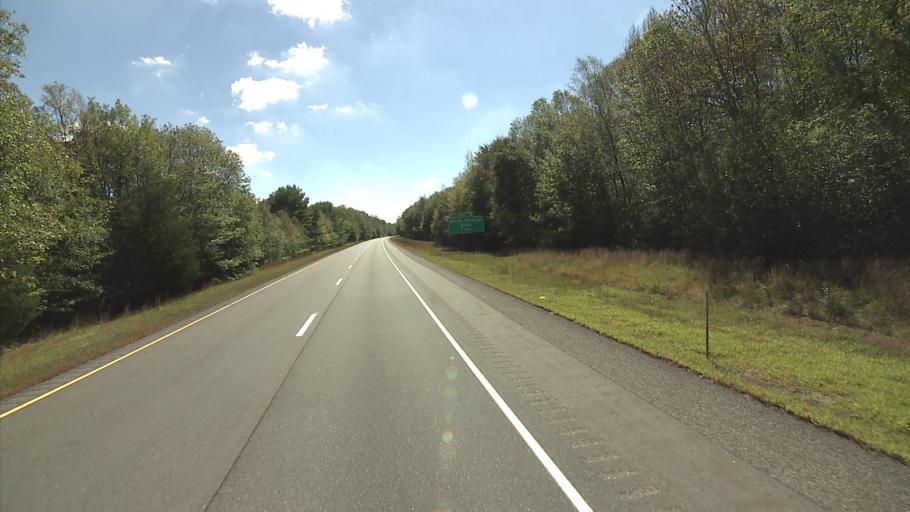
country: US
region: Connecticut
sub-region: New London County
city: Colchester
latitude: 41.5205
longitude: -72.3047
